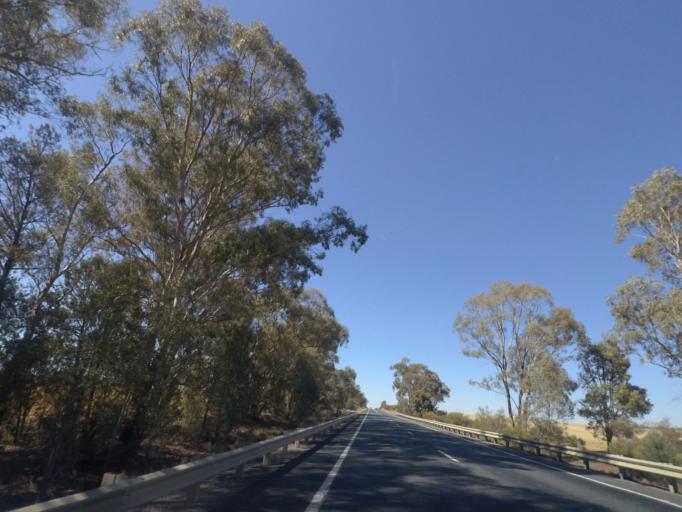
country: AU
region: New South Wales
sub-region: Bland
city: West Wyalong
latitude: -34.1764
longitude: 147.1141
